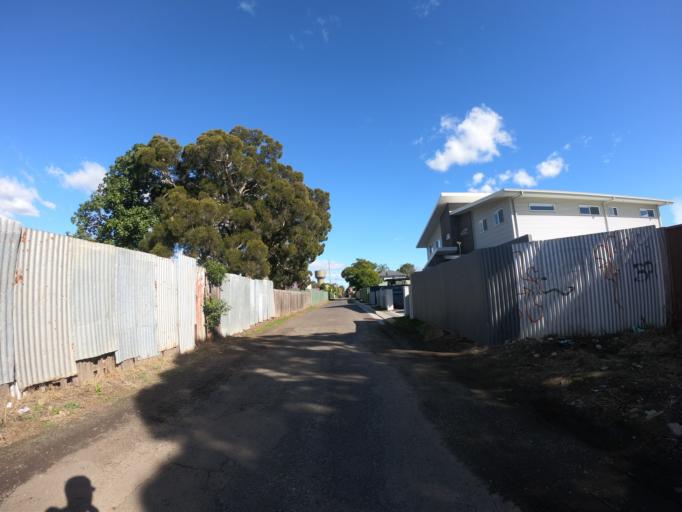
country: AU
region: New South Wales
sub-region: Hawkesbury
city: South Windsor
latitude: -33.6222
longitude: 150.8049
